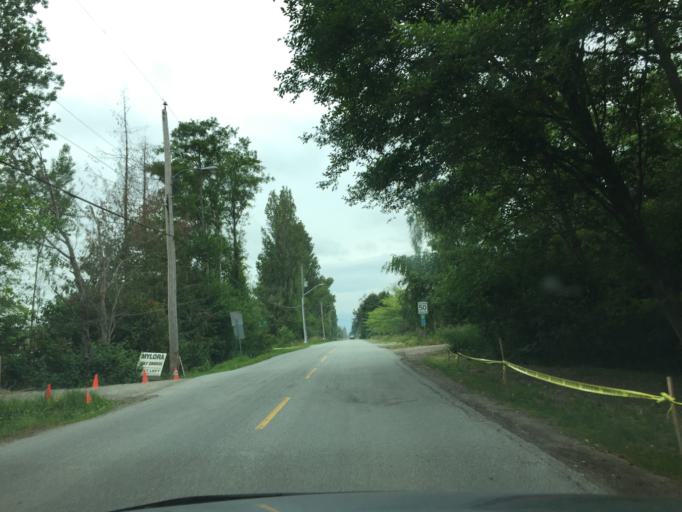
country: CA
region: British Columbia
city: Ladner
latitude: 49.1404
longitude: -123.0808
